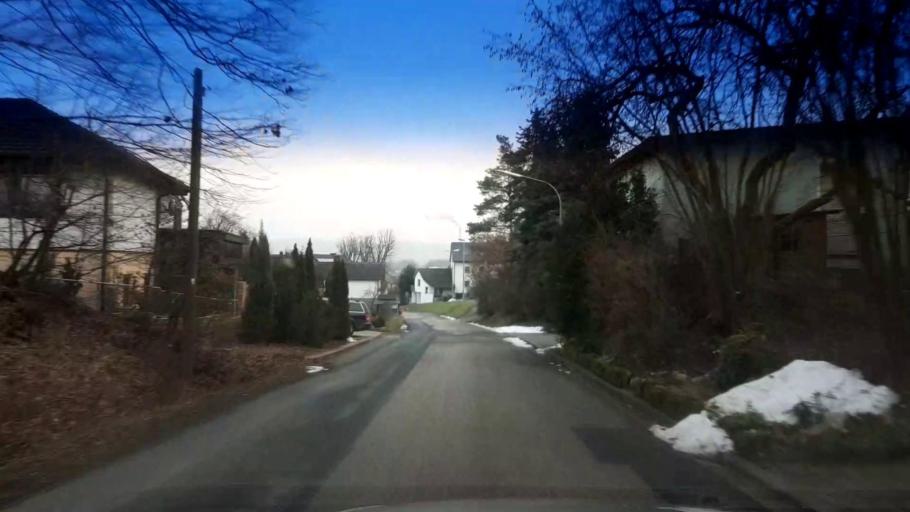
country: DE
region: Bavaria
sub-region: Upper Franconia
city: Hallerndorf
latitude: 49.7739
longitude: 10.9970
